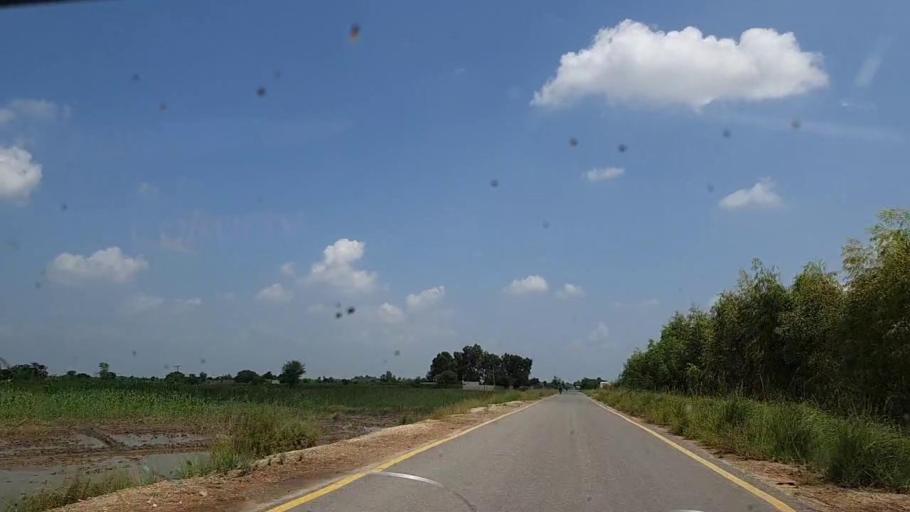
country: PK
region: Sindh
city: Tharu Shah
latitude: 26.9740
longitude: 68.0885
